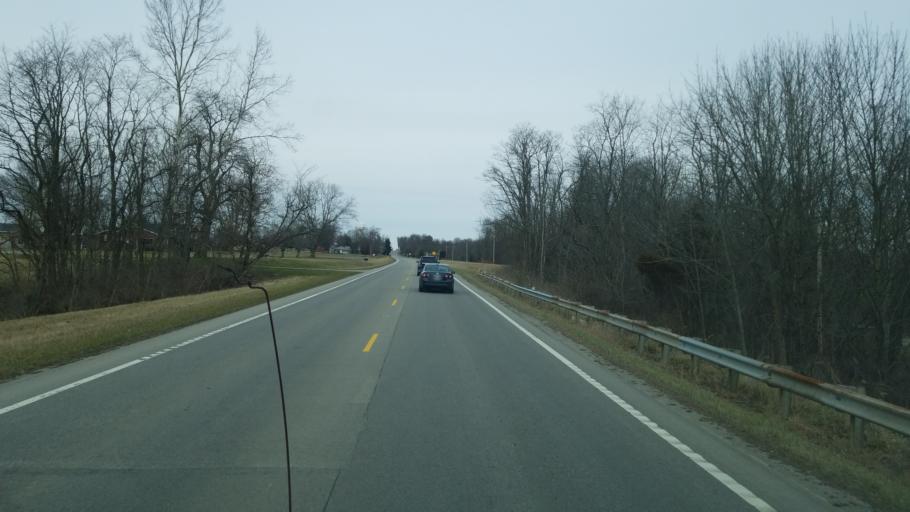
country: US
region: Ohio
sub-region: Highland County
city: Hillsboro
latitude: 39.1266
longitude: -83.6713
